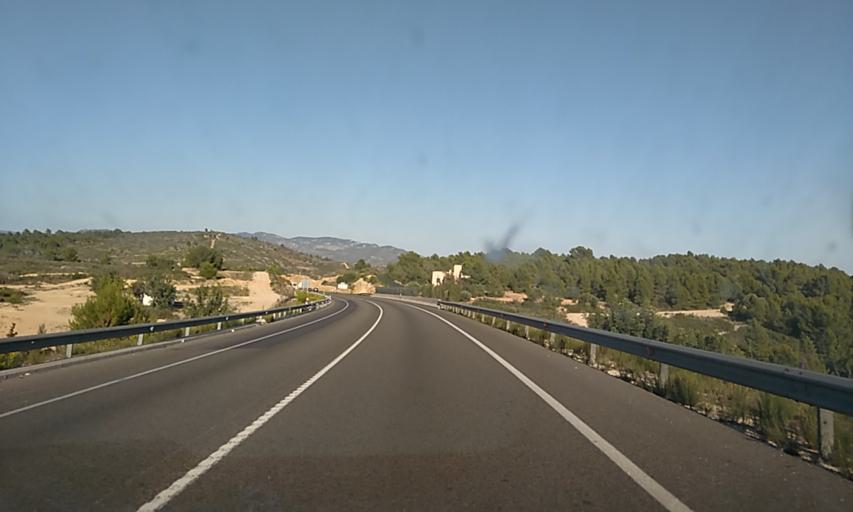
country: ES
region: Valencia
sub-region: Provincia de Castello
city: Torreblanca
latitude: 40.2229
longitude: 0.1741
